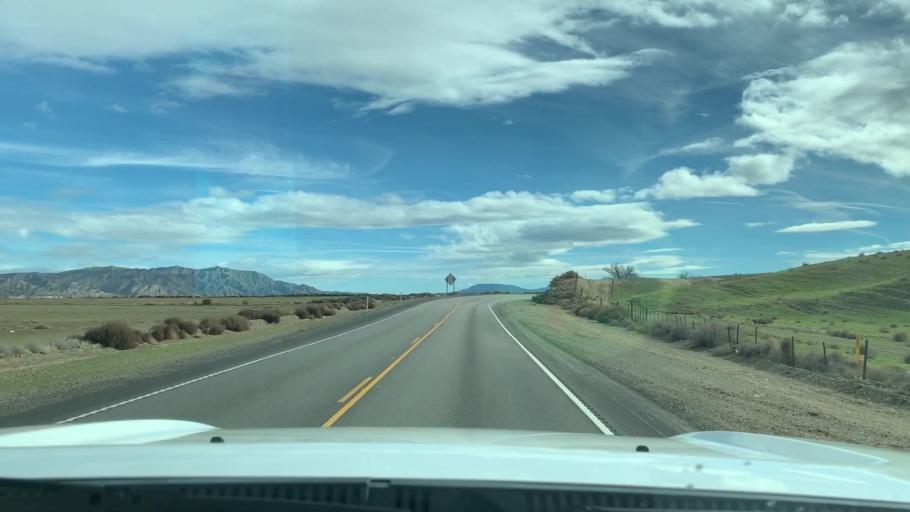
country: US
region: California
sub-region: Kern County
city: Taft Heights
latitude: 34.9641
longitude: -119.7246
